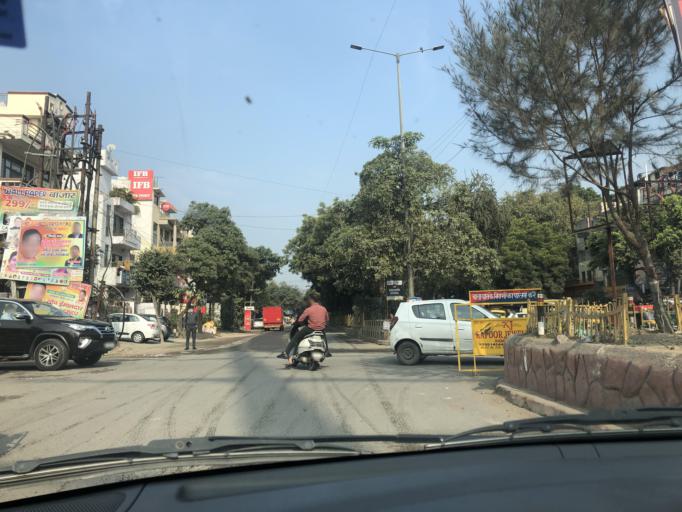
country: IN
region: Uttar Pradesh
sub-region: Gautam Buddha Nagar
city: Noida
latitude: 28.6468
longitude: 77.3597
